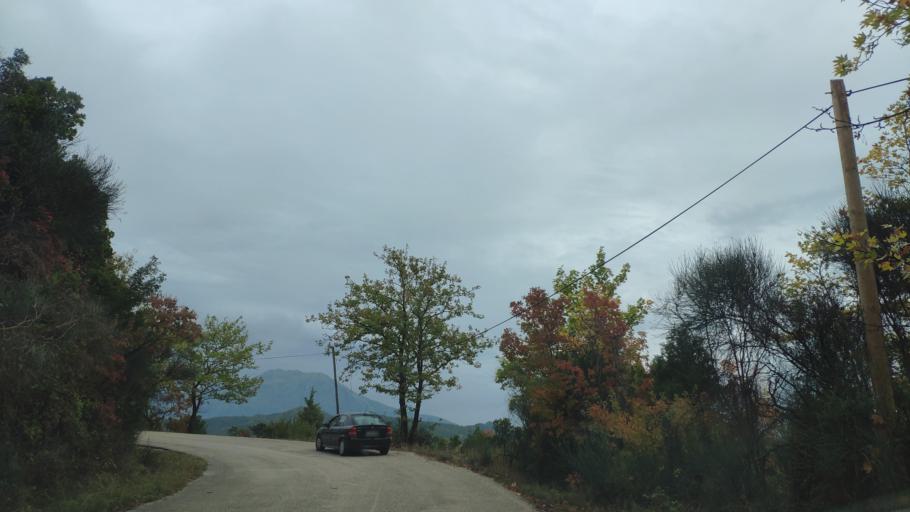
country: GR
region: Epirus
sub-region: Nomos Thesprotias
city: Paramythia
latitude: 39.4685
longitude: 20.6713
